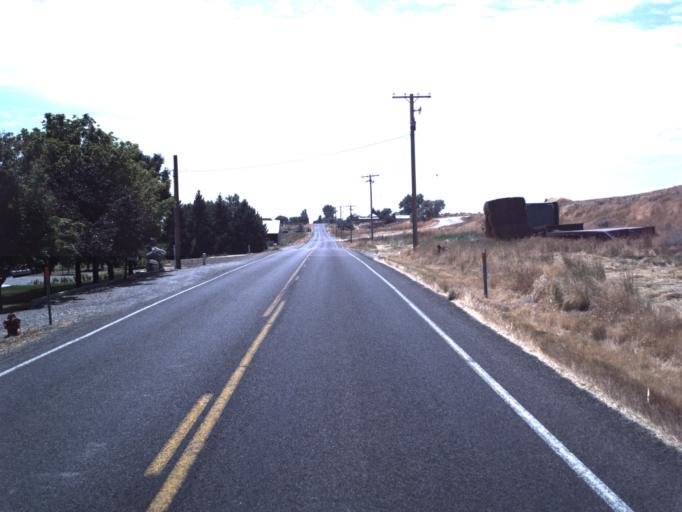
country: US
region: Utah
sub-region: Box Elder County
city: Tremonton
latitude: 41.6664
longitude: -112.2965
